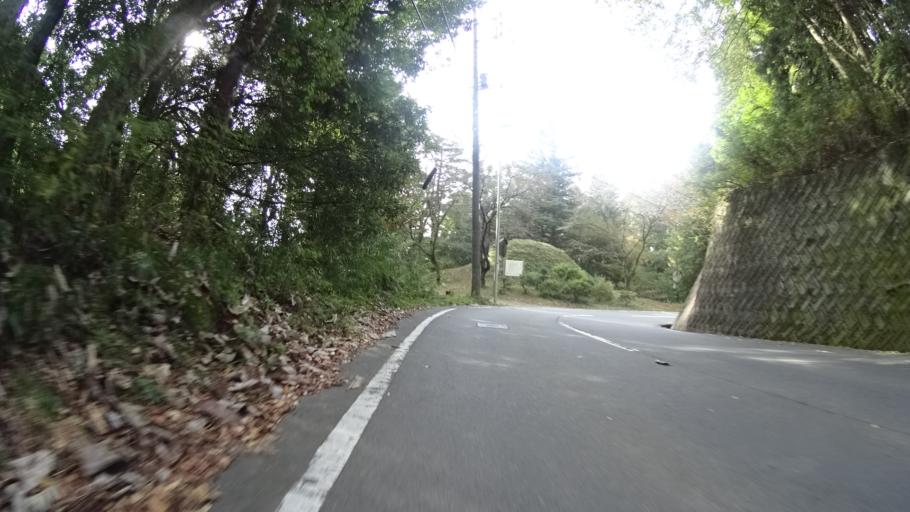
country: JP
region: Yamanashi
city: Uenohara
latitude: 35.6260
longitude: 139.0255
